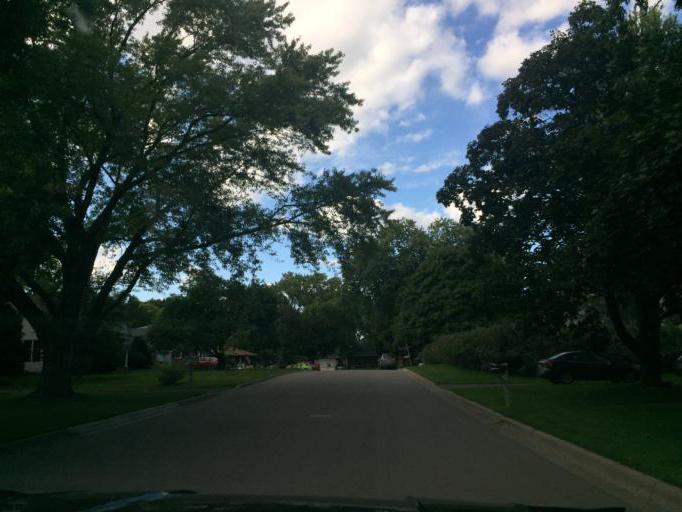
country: US
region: Minnesota
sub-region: Ramsey County
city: Roseville
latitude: 45.0079
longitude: -93.1430
